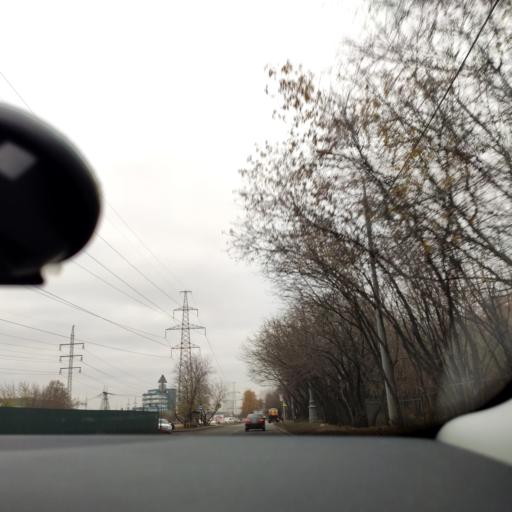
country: RU
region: Moscow
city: Kapotnya
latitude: 55.6613
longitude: 37.8105
